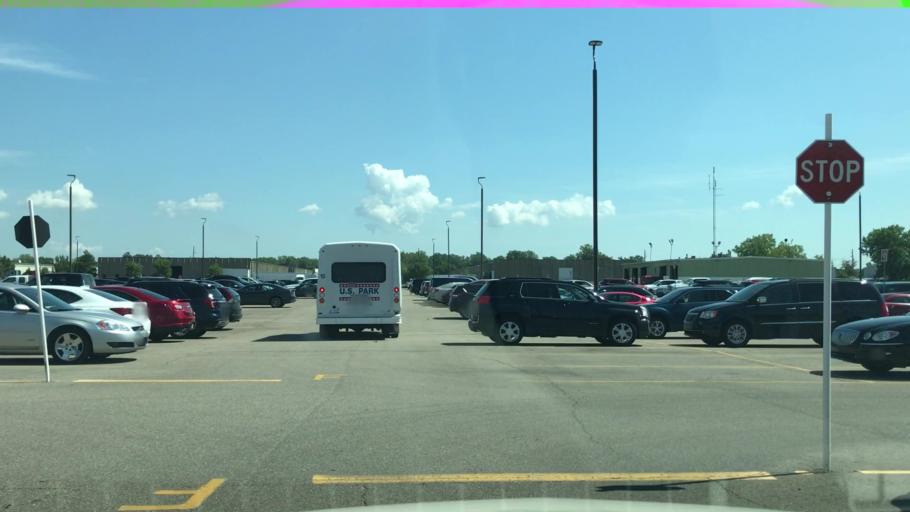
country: US
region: Michigan
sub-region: Wayne County
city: Taylor
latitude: 42.2345
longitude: -83.3229
